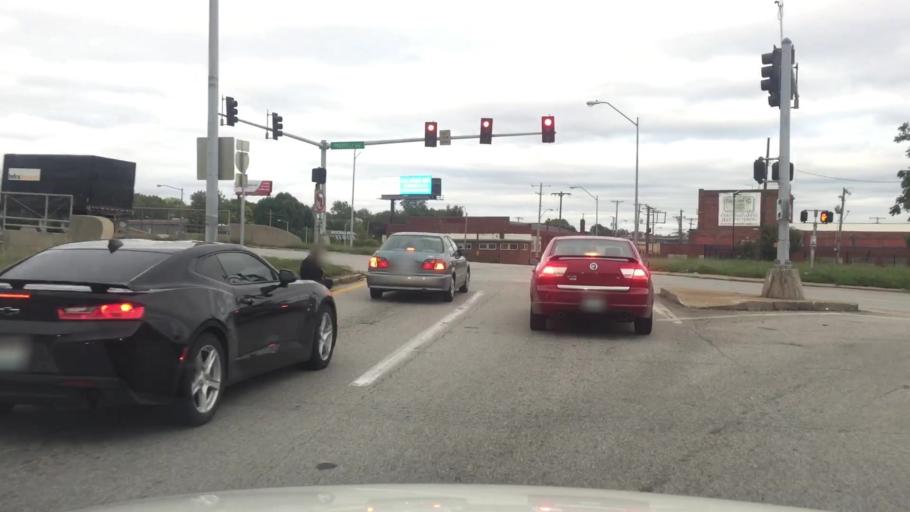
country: US
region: Missouri
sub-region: Jackson County
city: Kansas City
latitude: 39.0959
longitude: -94.5518
